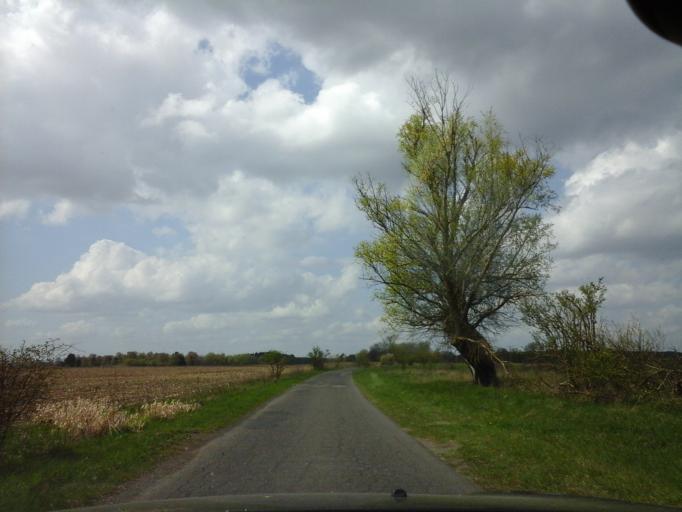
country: PL
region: West Pomeranian Voivodeship
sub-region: Powiat stargardzki
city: Dobrzany
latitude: 53.3311
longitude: 15.4092
